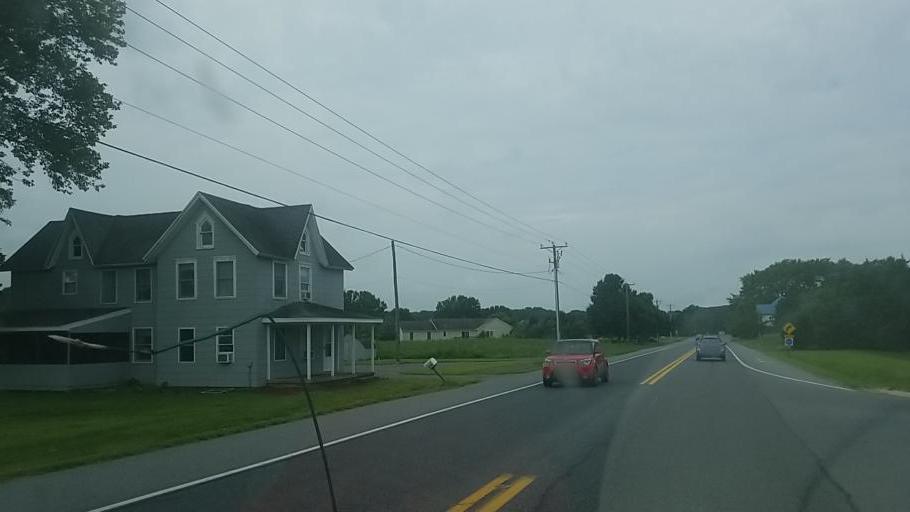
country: US
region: Delaware
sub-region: Sussex County
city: Long Neck
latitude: 38.5537
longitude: -75.1887
